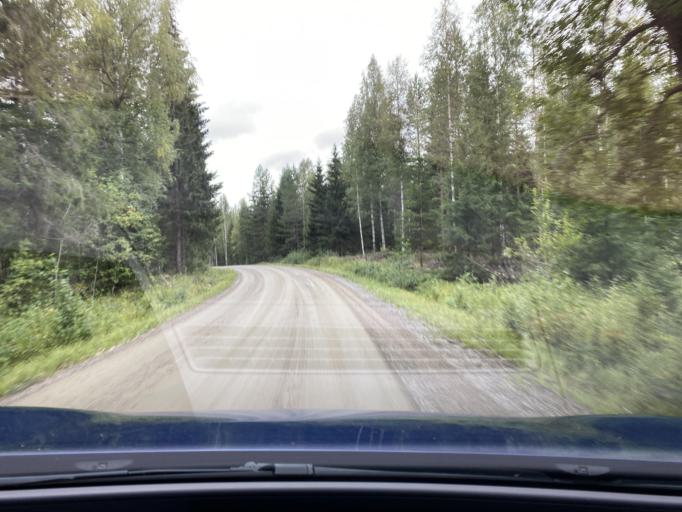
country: FI
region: Pirkanmaa
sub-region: Lounais-Pirkanmaa
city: Punkalaidun
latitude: 61.1940
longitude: 23.1814
